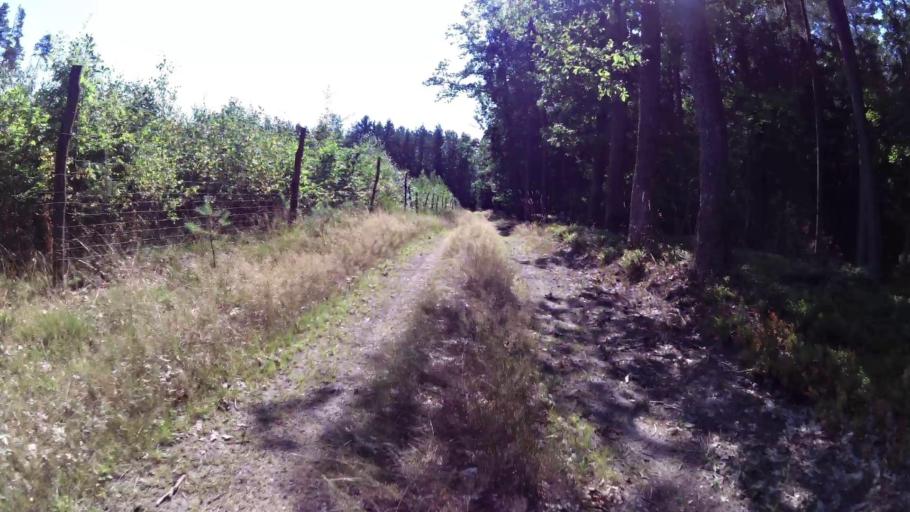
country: PL
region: West Pomeranian Voivodeship
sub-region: Powiat drawski
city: Czaplinek
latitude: 53.4478
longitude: 16.2261
